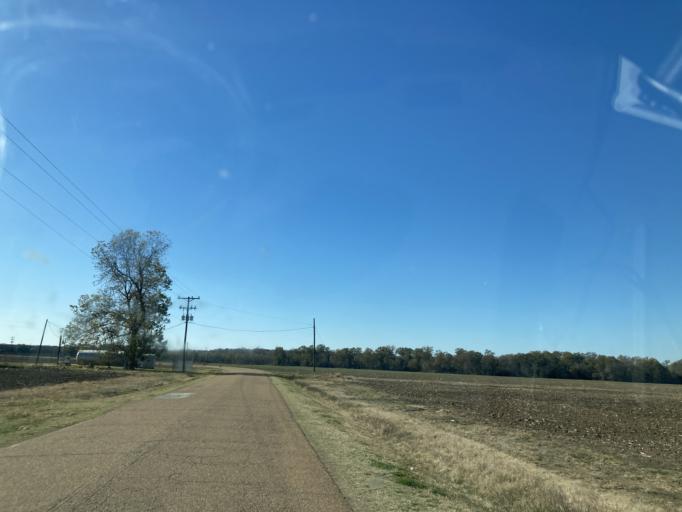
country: US
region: Mississippi
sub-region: Yazoo County
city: Yazoo City
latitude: 32.8993
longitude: -90.4509
